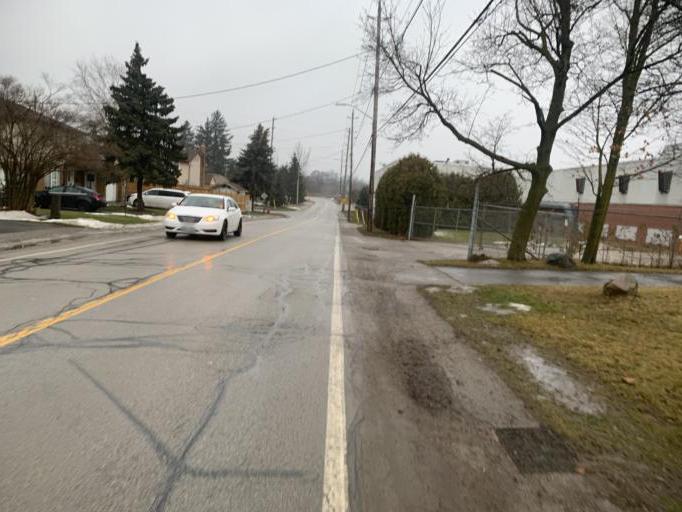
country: CA
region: Ontario
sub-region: Halton
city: Milton
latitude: 43.6573
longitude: -79.9244
